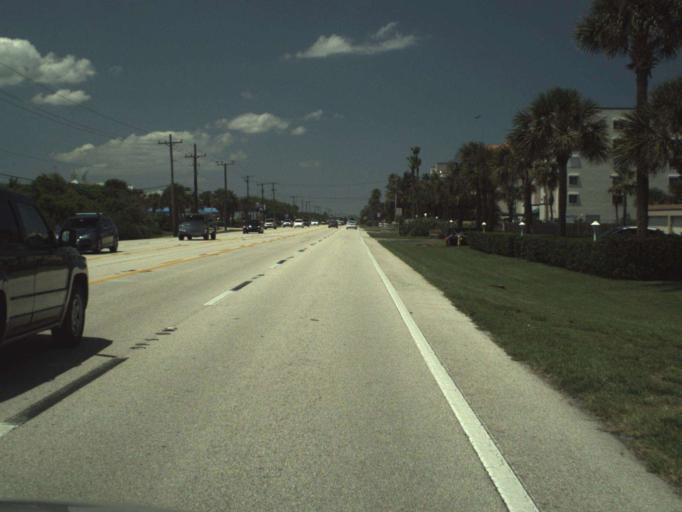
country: US
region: Florida
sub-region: Brevard County
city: Indialantic
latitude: 28.1064
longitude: -80.5716
